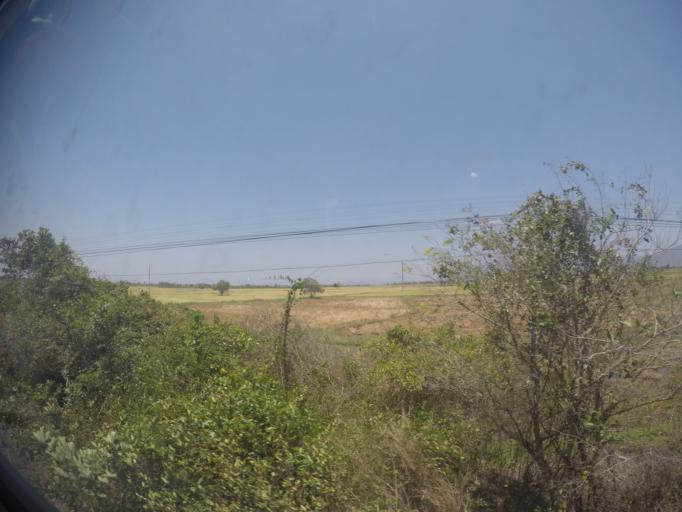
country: VN
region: Binh Thuan
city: Cho Lau
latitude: 11.2408
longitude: 108.4789
